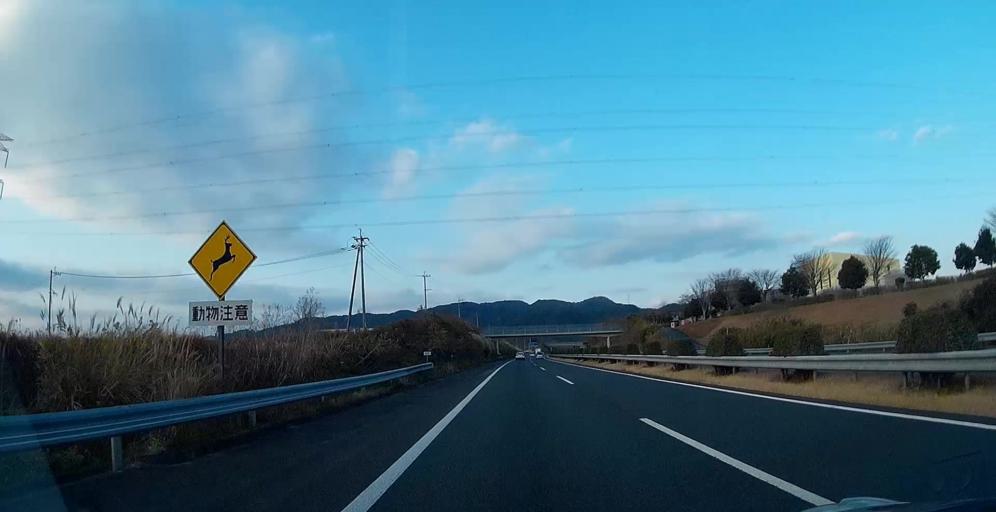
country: JP
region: Kumamoto
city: Matsubase
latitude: 32.6609
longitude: 130.7117
